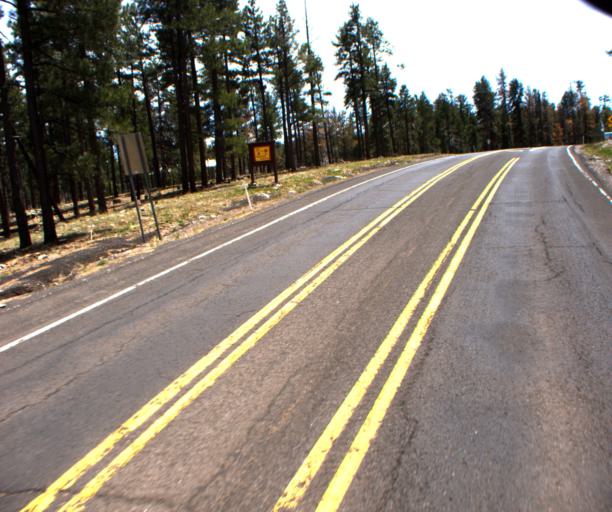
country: US
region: Arizona
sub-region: Coconino County
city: Kachina Village
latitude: 35.0391
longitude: -111.7335
